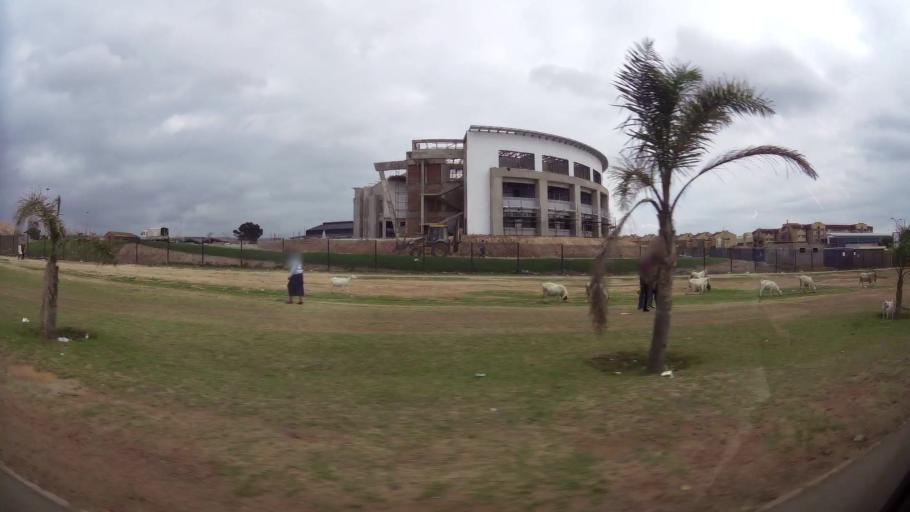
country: ZA
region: Eastern Cape
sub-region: Nelson Mandela Bay Metropolitan Municipality
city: Port Elizabeth
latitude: -33.8794
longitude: 25.5634
